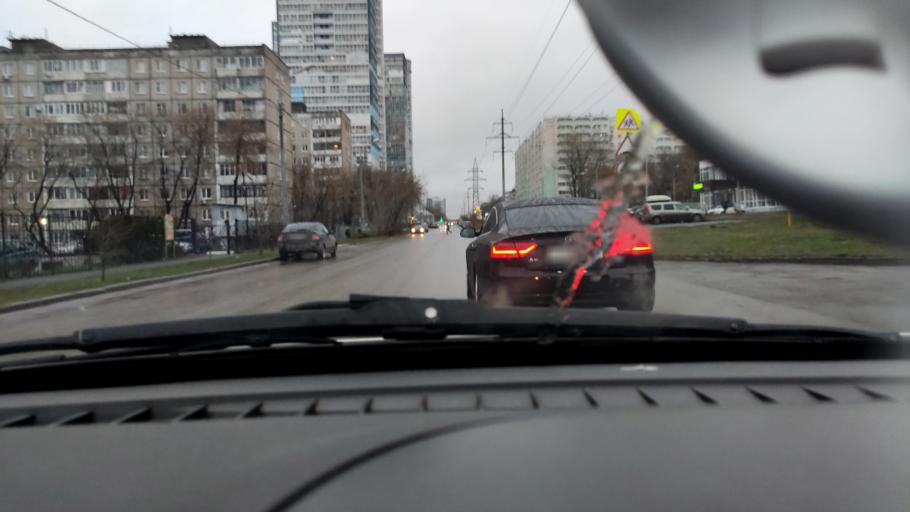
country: RU
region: Perm
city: Kondratovo
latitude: 57.9684
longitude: 56.1647
